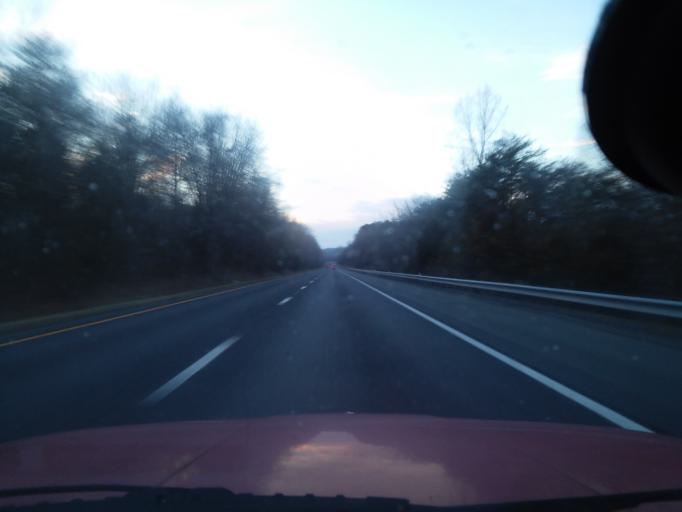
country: US
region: Virginia
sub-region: Fluvanna County
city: Lake Monticello
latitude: 38.0039
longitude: -78.3573
